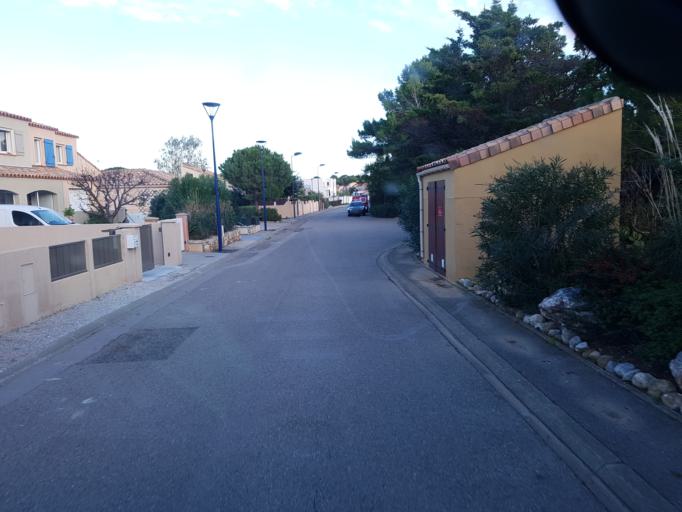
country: FR
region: Languedoc-Roussillon
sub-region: Departement de l'Aude
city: Leucate
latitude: 42.9363
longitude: 3.0246
